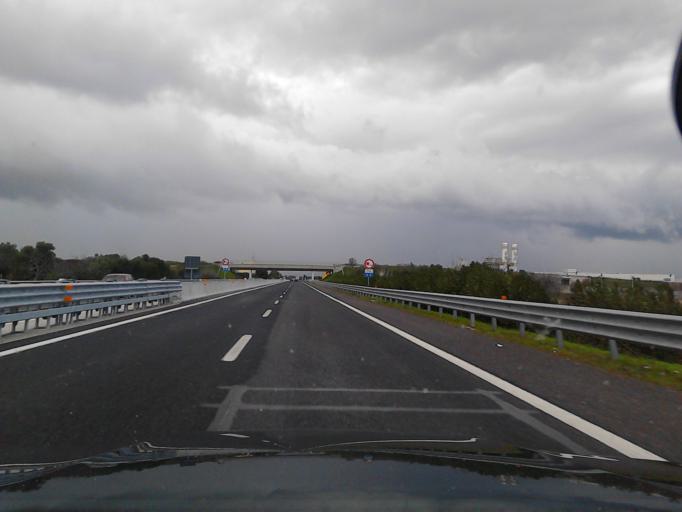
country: IT
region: Apulia
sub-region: Provincia di Bari
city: Modugno
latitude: 41.0973
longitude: 16.7641
